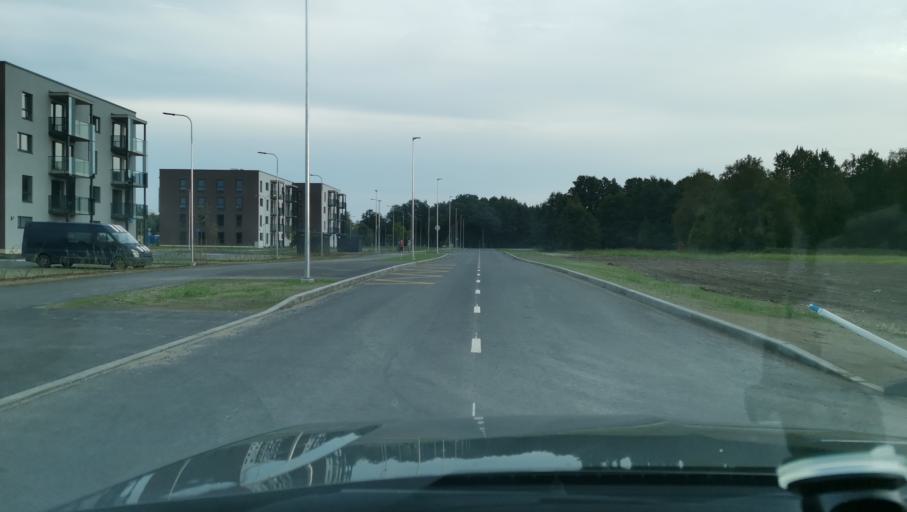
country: EE
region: Harju
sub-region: Saue vald
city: Laagri
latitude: 59.4197
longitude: 24.6298
